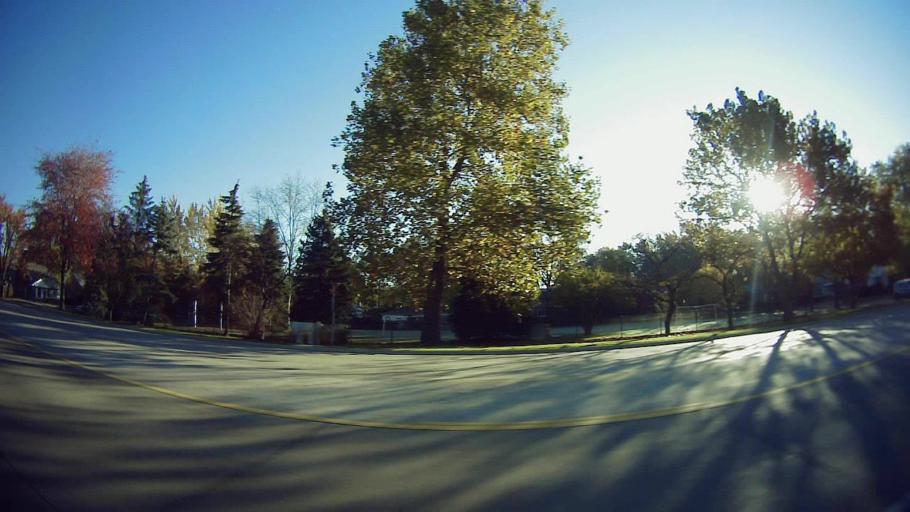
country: US
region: Michigan
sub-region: Oakland County
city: Huntington Woods
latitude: 42.4774
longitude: -83.1829
